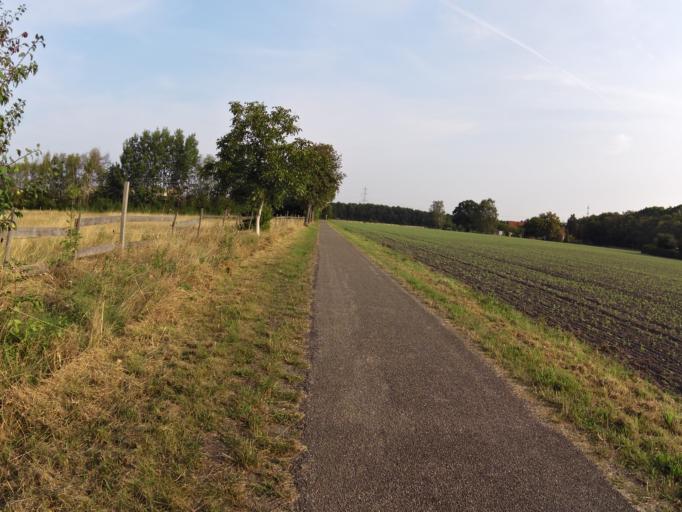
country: DE
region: North Rhine-Westphalia
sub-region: Regierungsbezirk Detmold
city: Petershagen
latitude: 52.3942
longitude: 8.9645
